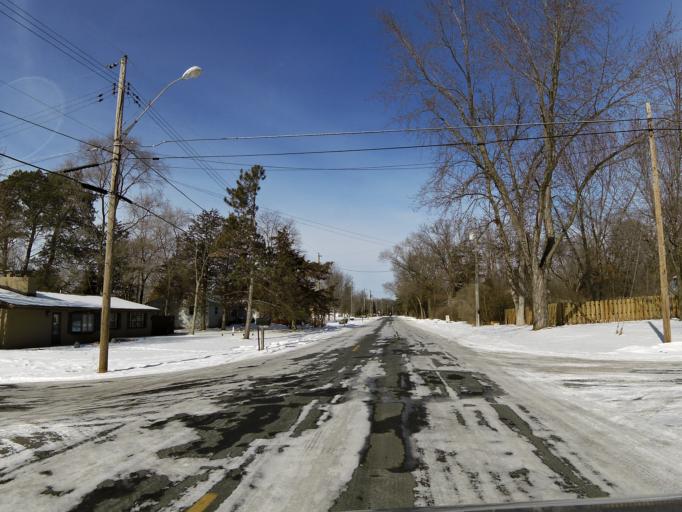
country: US
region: Minnesota
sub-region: Washington County
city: Lake Saint Croix Beach
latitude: 44.9269
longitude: -92.7686
